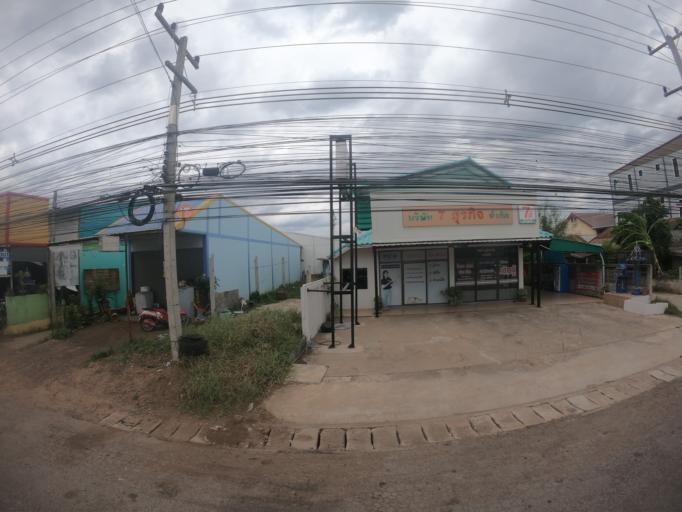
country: TH
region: Nakhon Ratchasima
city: Chok Chai
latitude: 14.7428
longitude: 102.1649
